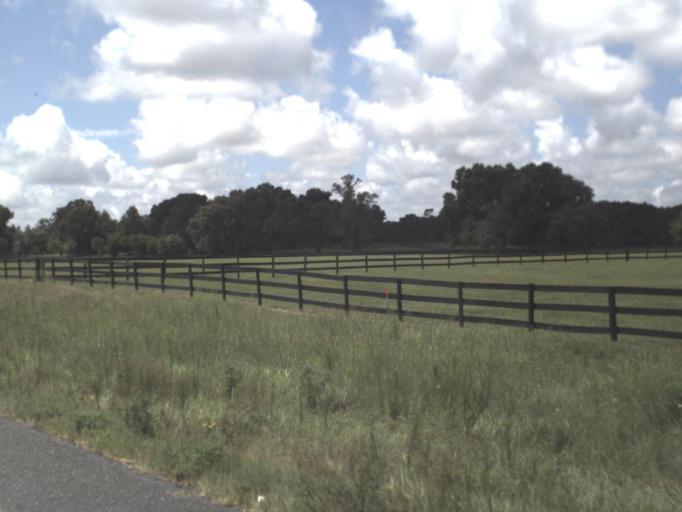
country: US
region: Florida
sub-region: Gilchrist County
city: Trenton
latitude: 29.8315
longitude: -82.8674
